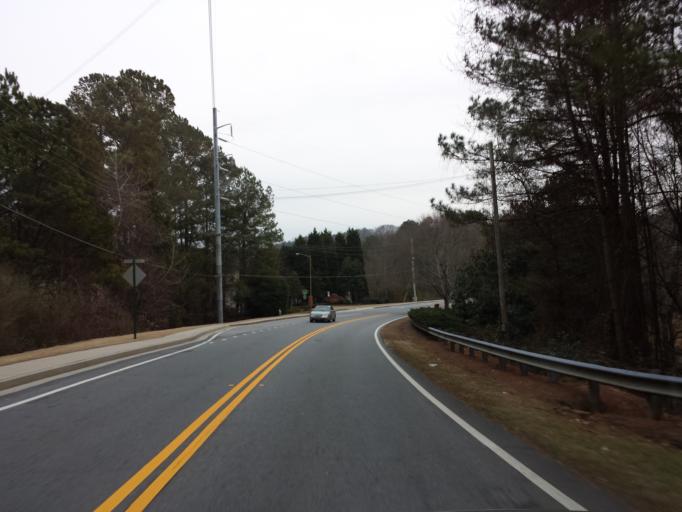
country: US
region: Georgia
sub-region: Fulton County
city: Roswell
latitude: 34.0176
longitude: -84.4024
